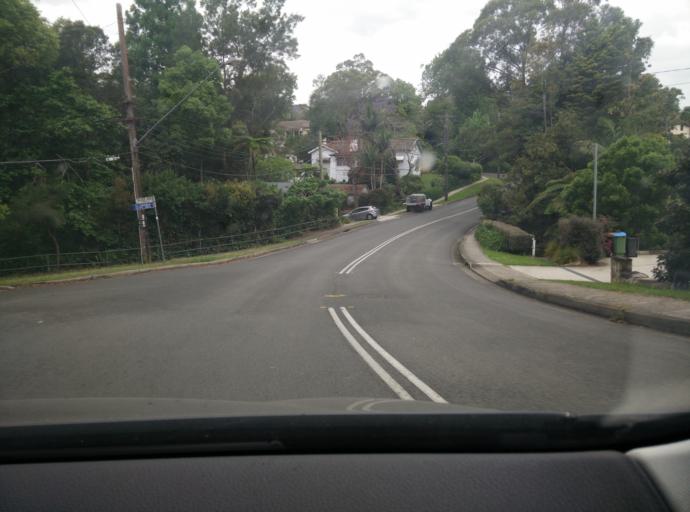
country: AU
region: New South Wales
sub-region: Ku-ring-gai
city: East Lindfield
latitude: -33.7727
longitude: 151.1756
